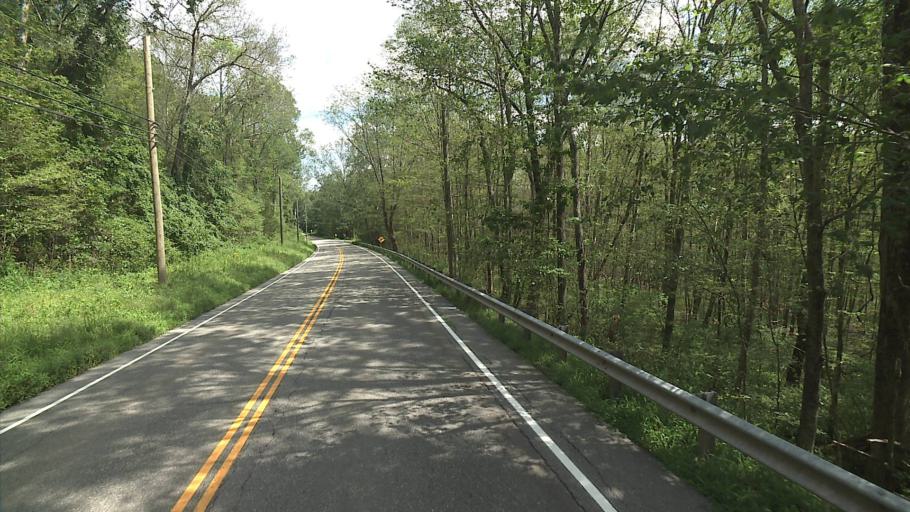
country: US
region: Connecticut
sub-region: Windham County
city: Windham
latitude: 41.8126
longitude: -72.1109
